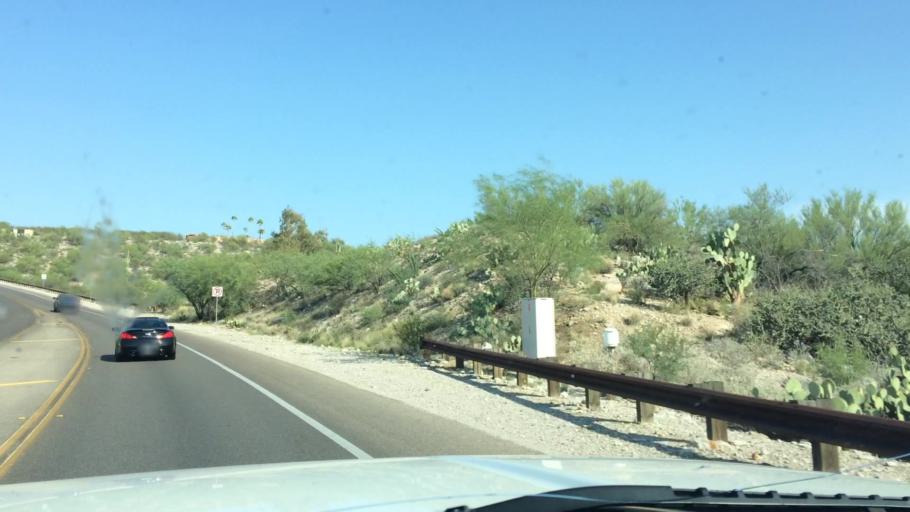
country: US
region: Arizona
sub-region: Pima County
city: Catalina Foothills
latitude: 32.3062
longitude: -110.8686
